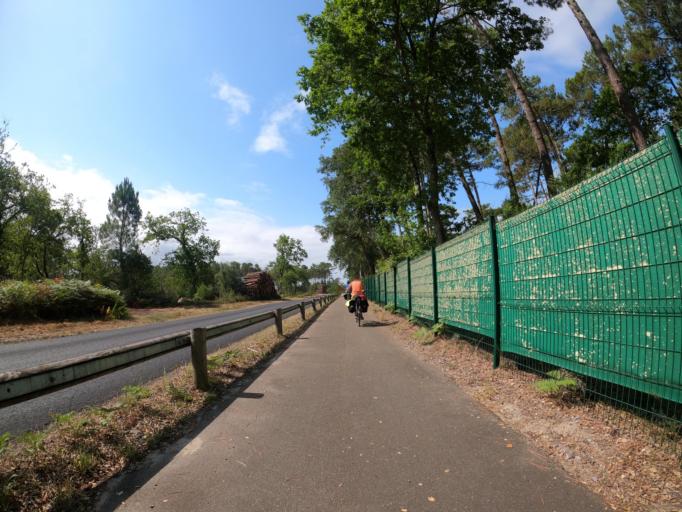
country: FR
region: Aquitaine
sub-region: Departement des Landes
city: Leon
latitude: 43.9058
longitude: -1.3623
